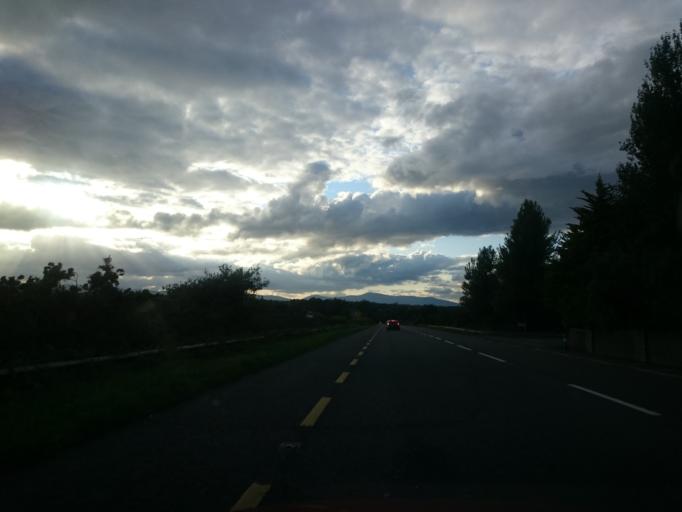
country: IE
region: Leinster
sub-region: Loch Garman
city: Enniscorthy
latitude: 52.4486
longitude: -6.5477
